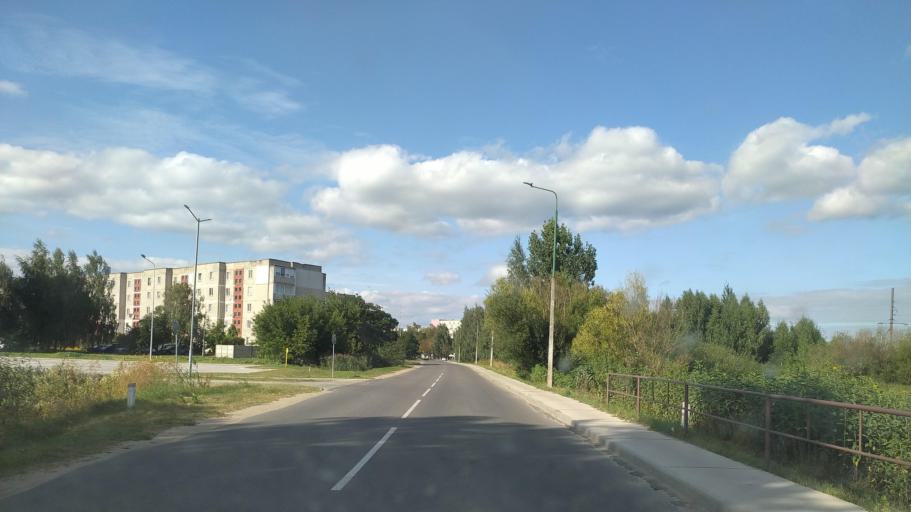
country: BY
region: Brest
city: Byaroza
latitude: 52.5348
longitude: 24.9955
